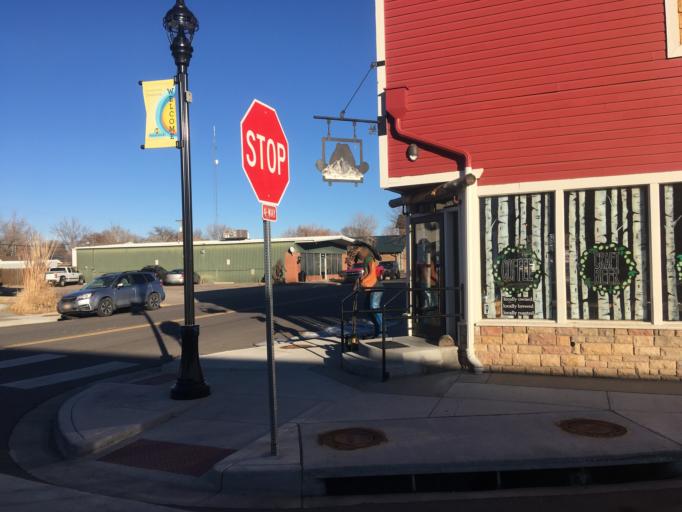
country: US
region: Colorado
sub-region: Weld County
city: Frederick
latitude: 40.0985
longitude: -104.9383
